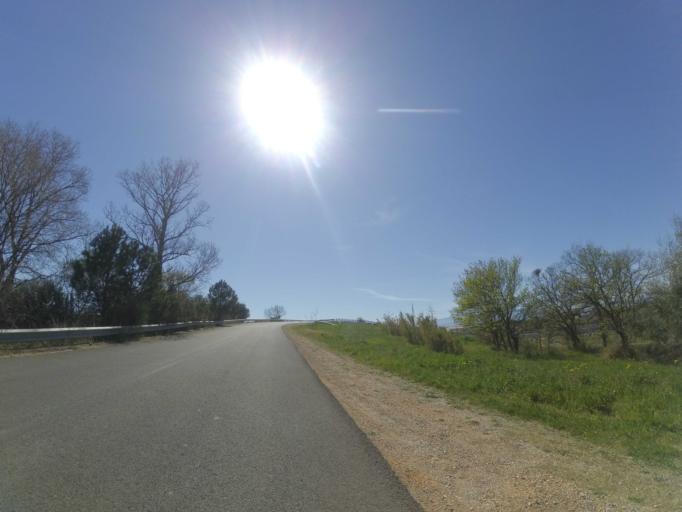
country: FR
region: Languedoc-Roussillon
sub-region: Departement des Pyrenees-Orientales
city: Toulouges
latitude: 42.6772
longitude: 2.8637
